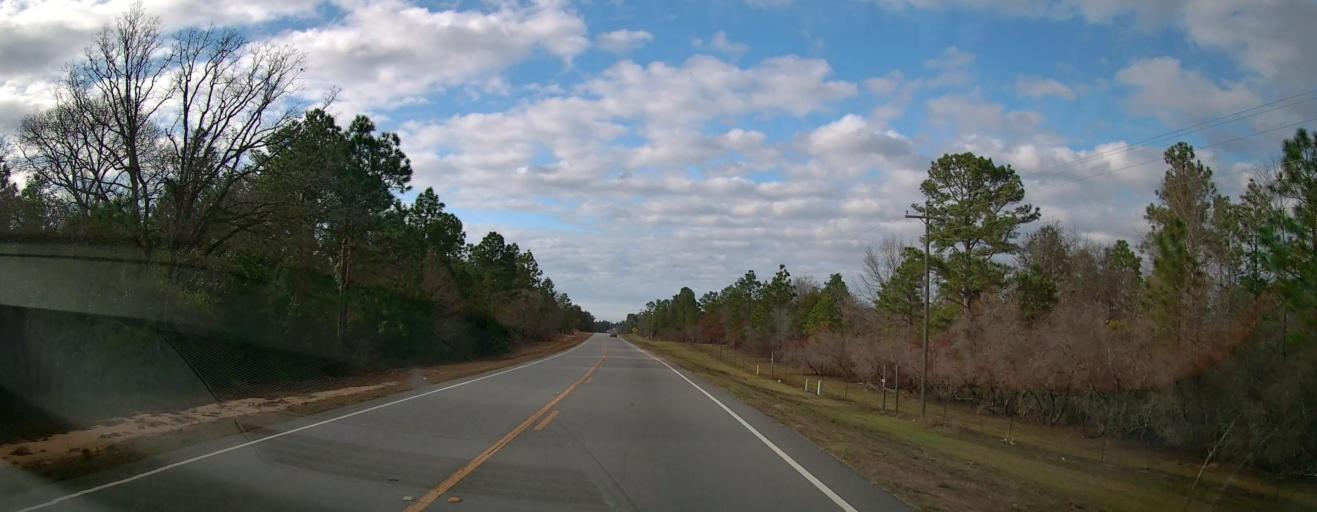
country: US
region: Georgia
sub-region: Marion County
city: Buena Vista
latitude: 32.4860
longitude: -84.5480
